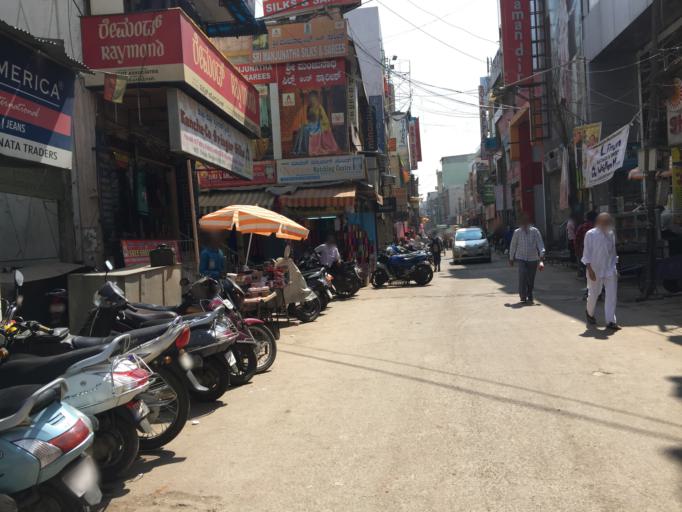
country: IN
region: Karnataka
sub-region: Bangalore Urban
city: Bangalore
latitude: 12.9690
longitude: 77.5771
